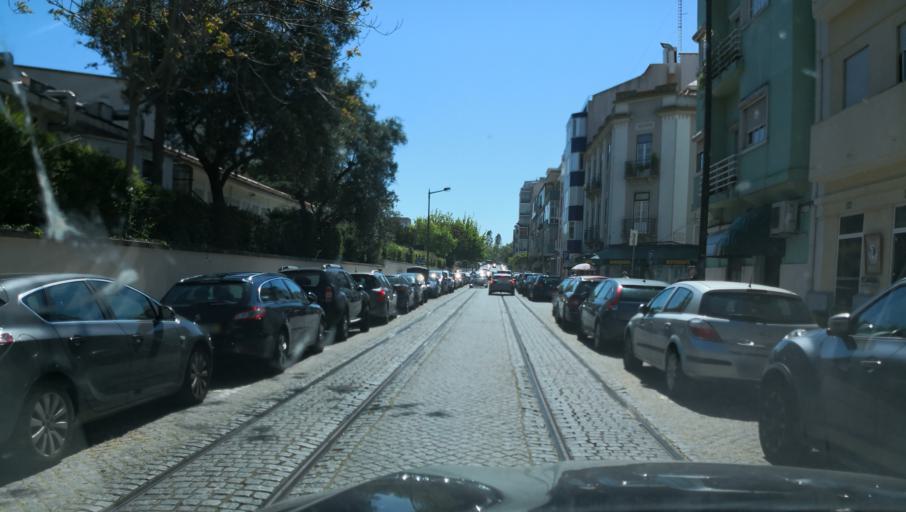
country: PT
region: Lisbon
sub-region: Lisbon
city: Lisbon
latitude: 38.7397
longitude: -9.1638
